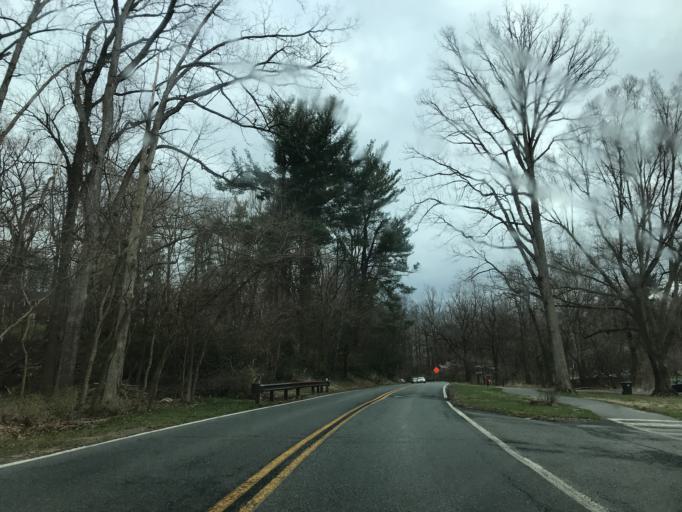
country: US
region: Maryland
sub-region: Montgomery County
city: Silver Spring
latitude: 38.9983
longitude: -77.0097
